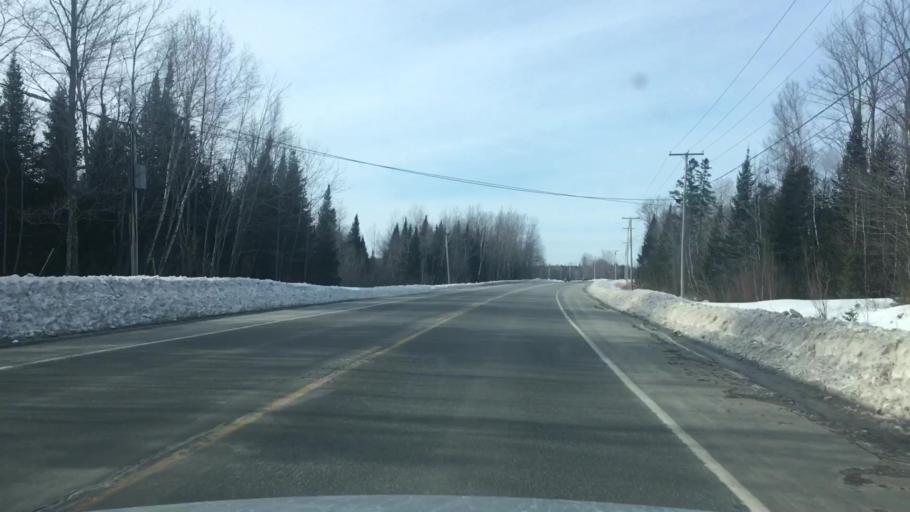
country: US
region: Maine
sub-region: Penobscot County
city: Kenduskeag
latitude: 44.9074
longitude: -68.8939
